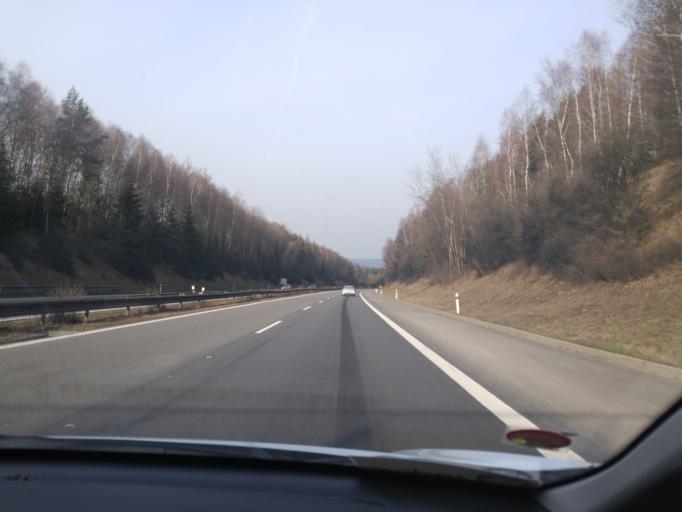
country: CZ
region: Vysocina
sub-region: Okres Pelhrimov
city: Zeliv
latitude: 49.5693
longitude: 15.2801
